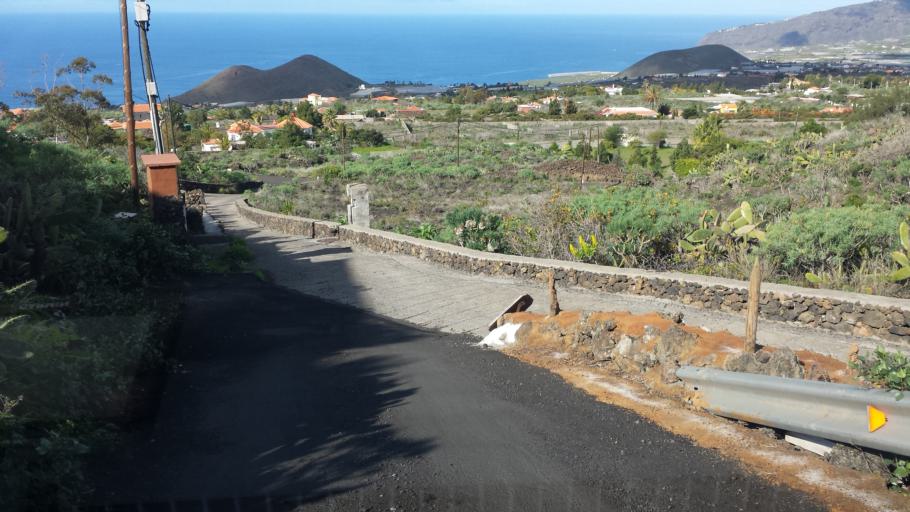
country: ES
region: Canary Islands
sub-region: Provincia de Santa Cruz de Tenerife
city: El Paso
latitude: 28.6114
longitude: -17.8908
